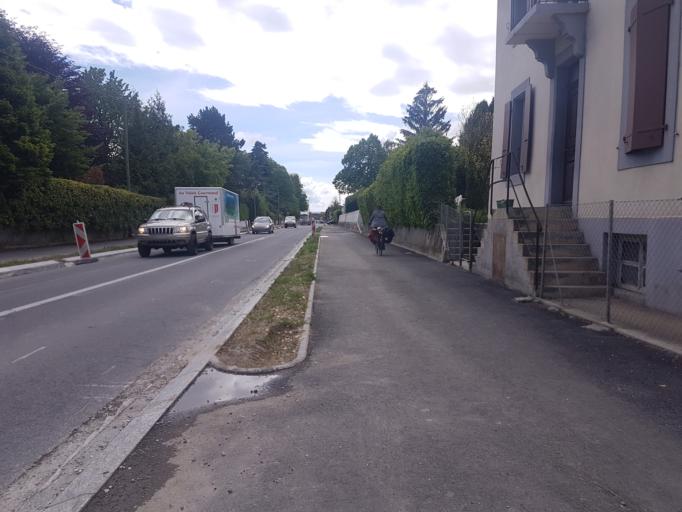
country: CH
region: Vaud
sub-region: Nyon District
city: Coppet
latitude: 46.3225
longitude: 6.1969
